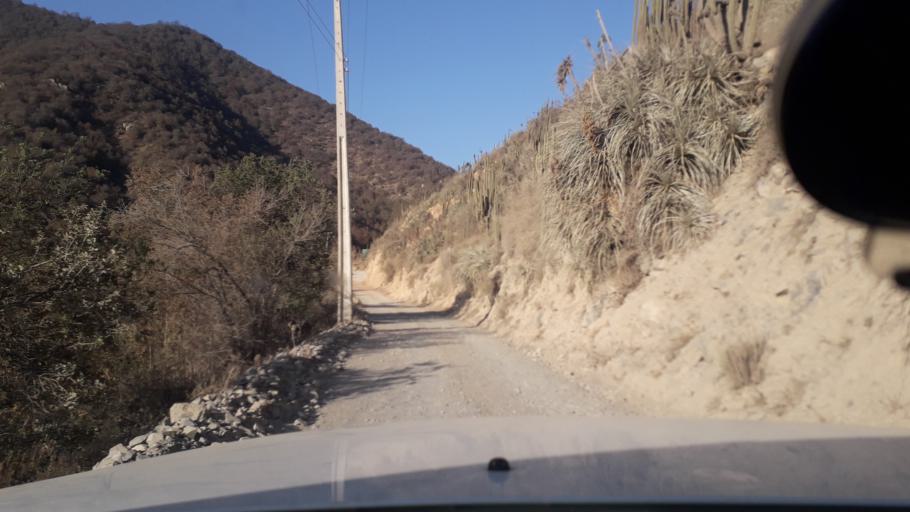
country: CL
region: Valparaiso
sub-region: Provincia de Marga Marga
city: Limache
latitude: -33.0525
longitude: -71.0800
